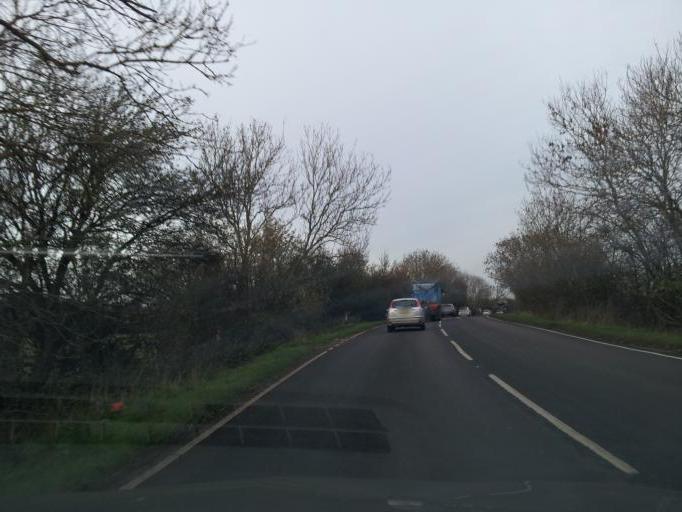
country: GB
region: England
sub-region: Buckinghamshire
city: Aylesbury
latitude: 51.8573
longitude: -0.7668
